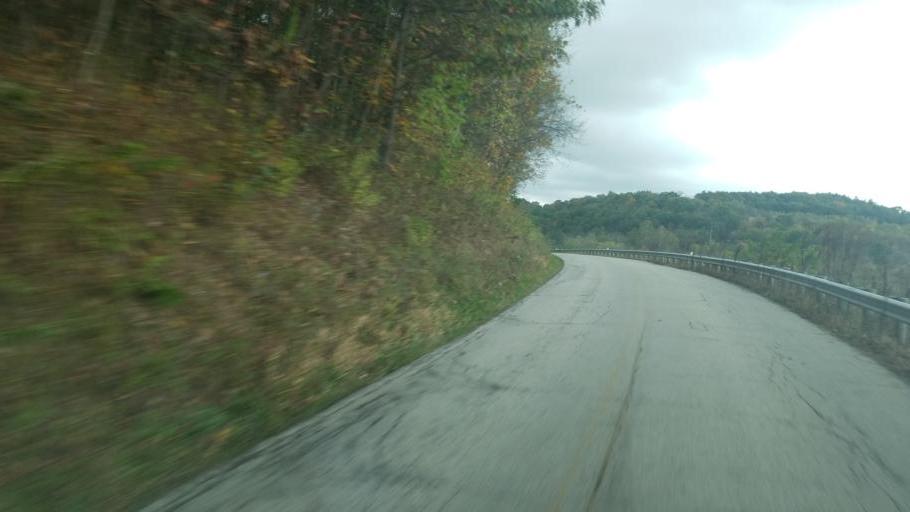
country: US
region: Ohio
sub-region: Ashland County
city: Loudonville
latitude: 40.5885
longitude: -82.1675
